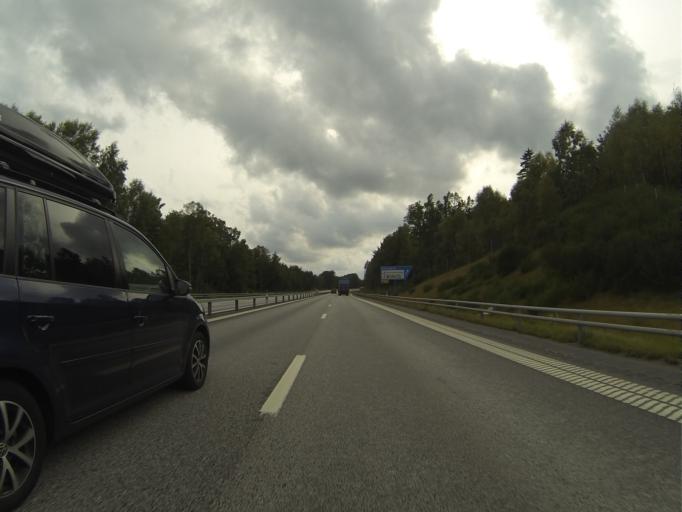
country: SE
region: Skane
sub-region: Horby Kommun
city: Hoerby
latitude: 55.9075
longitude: 13.7468
